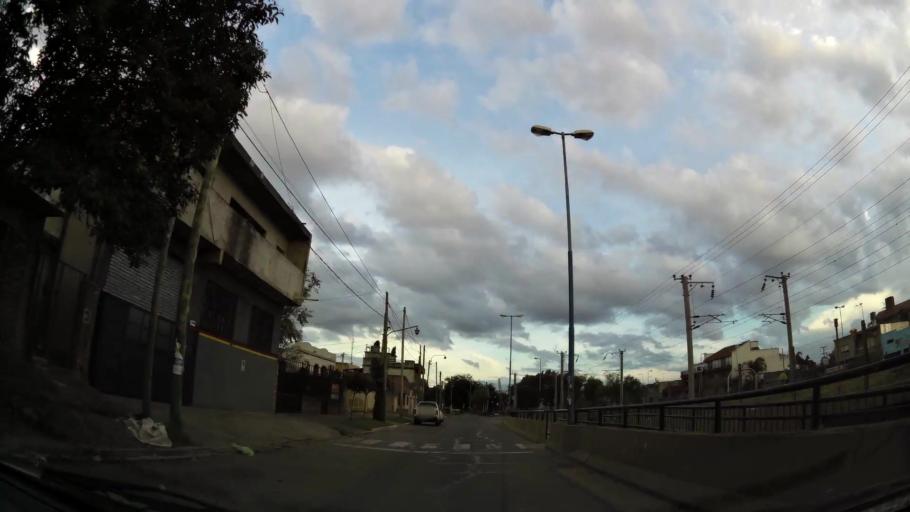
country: AR
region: Buenos Aires
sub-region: Partido de Quilmes
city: Quilmes
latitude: -34.7491
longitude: -58.2382
